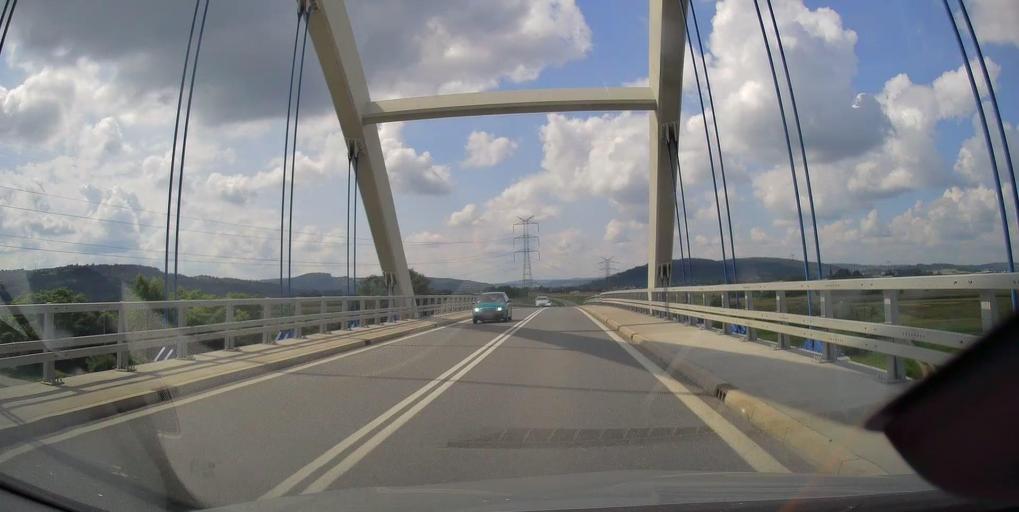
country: PL
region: Lesser Poland Voivodeship
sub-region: Powiat tarnowski
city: Wojnicz
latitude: 49.9517
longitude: 20.8502
